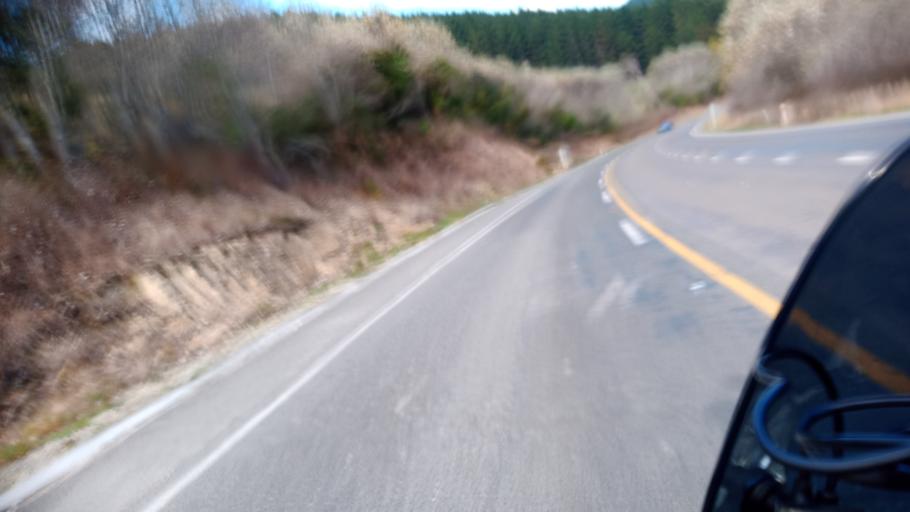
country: NZ
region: Gisborne
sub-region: Gisborne District
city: Gisborne
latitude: -38.8285
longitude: 177.9022
